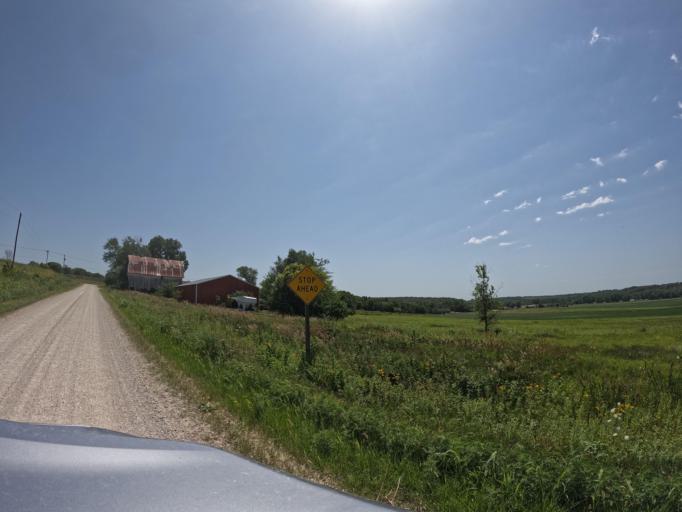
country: US
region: Iowa
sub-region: Henry County
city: Mount Pleasant
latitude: 40.9085
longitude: -91.5562
